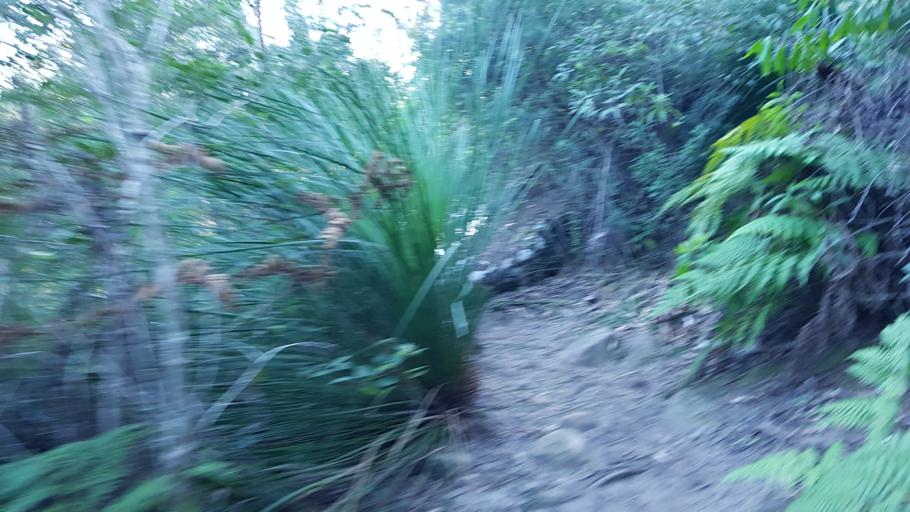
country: AU
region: New South Wales
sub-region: Lane Cove
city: Lane Cove West
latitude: -33.7989
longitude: 151.1463
